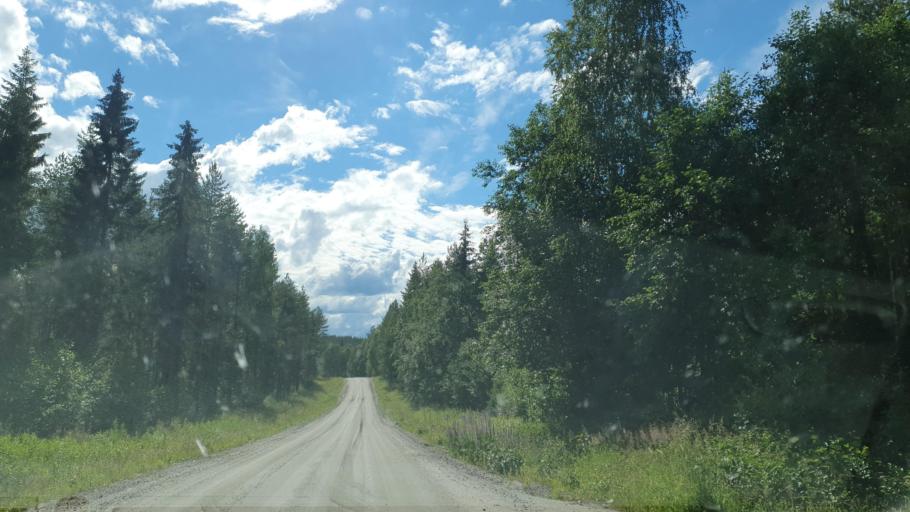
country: FI
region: Kainuu
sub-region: Kehys-Kainuu
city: Kuhmo
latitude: 64.1327
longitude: 29.6602
